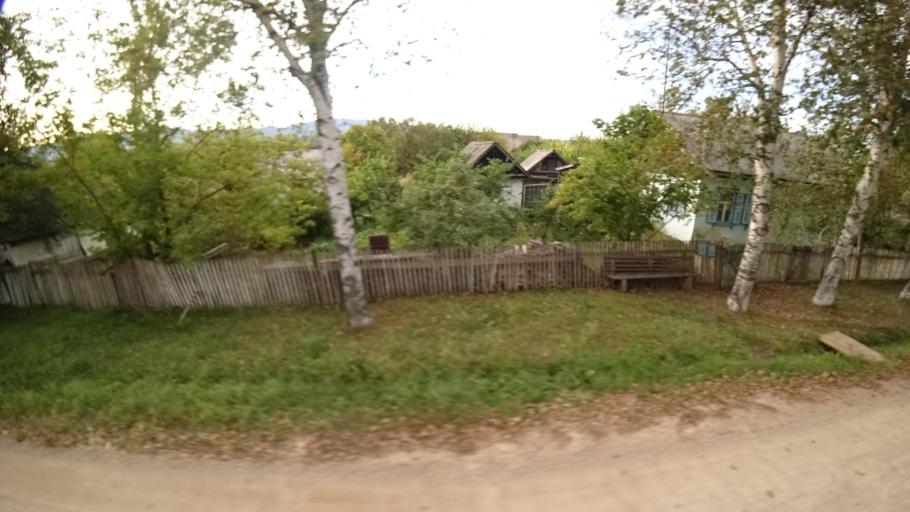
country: RU
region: Primorskiy
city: Yakovlevka
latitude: 44.4151
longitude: 133.4519
